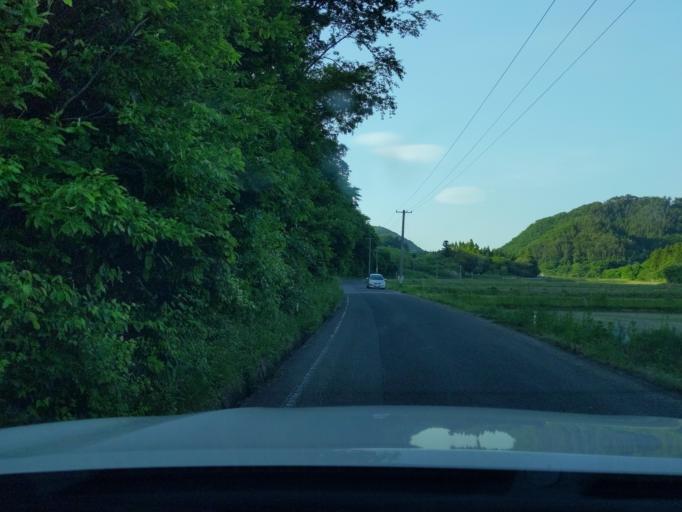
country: JP
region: Fukushima
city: Motomiya
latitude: 37.5042
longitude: 140.3255
